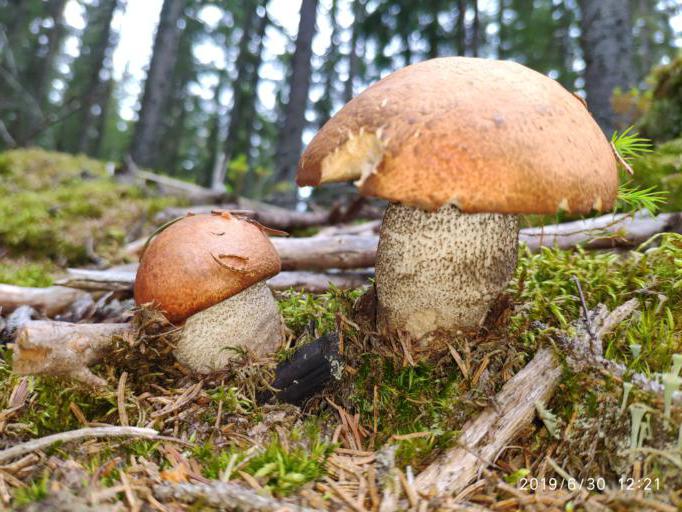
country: NO
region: Oppland
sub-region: Lunner
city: Grua
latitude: 60.2771
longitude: 10.7297
